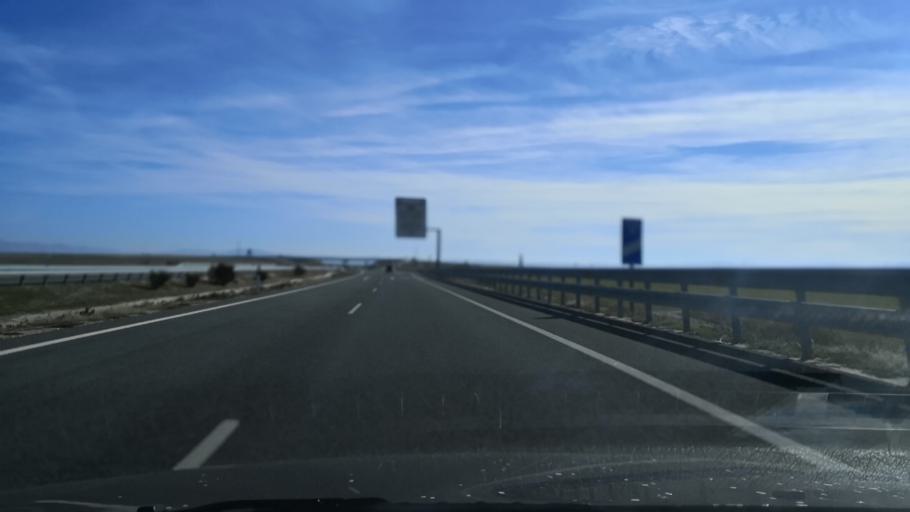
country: ES
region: Castille and Leon
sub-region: Provincia de Avila
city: Crespos
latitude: 40.8474
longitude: -4.9713
